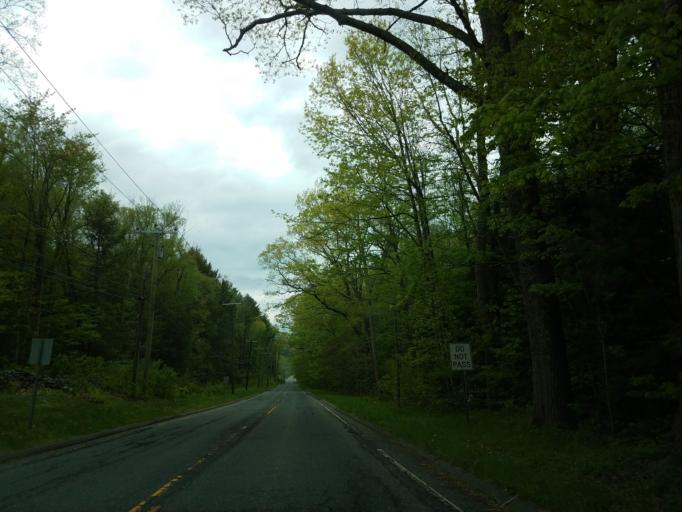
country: US
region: Connecticut
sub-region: Litchfield County
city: Winsted
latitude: 42.0102
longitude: -73.1096
